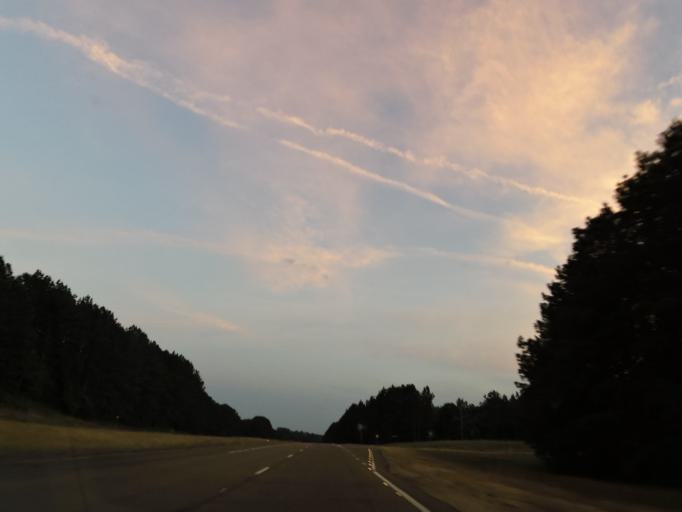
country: US
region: Mississippi
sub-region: Lauderdale County
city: Meridian Station
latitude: 32.6120
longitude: -88.4992
